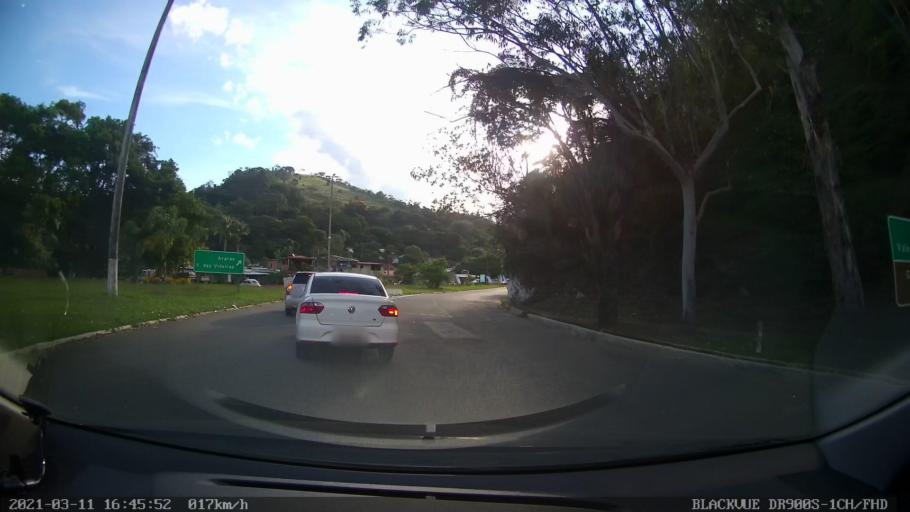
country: BR
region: Rio de Janeiro
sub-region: Petropolis
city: Petropolis
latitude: -22.4133
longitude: -43.1403
